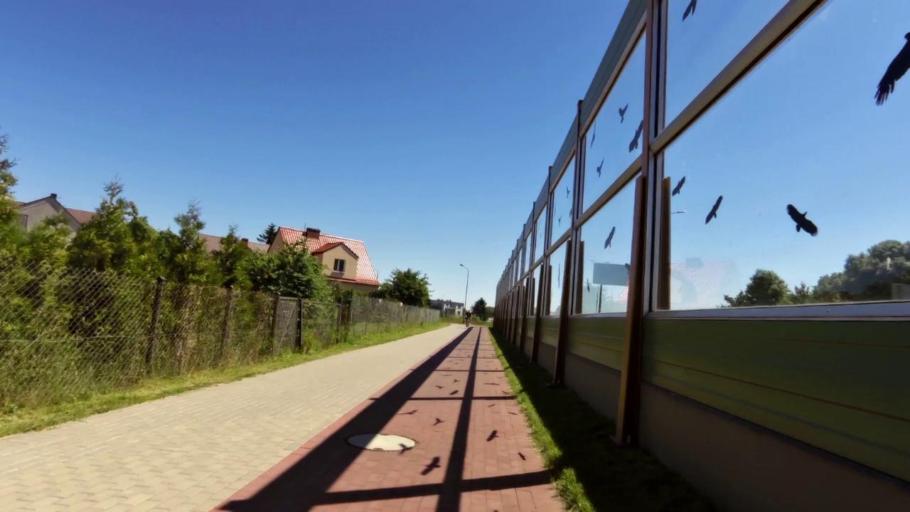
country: PL
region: West Pomeranian Voivodeship
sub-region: Powiat kolobrzeski
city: Kolobrzeg
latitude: 54.1635
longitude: 15.5517
